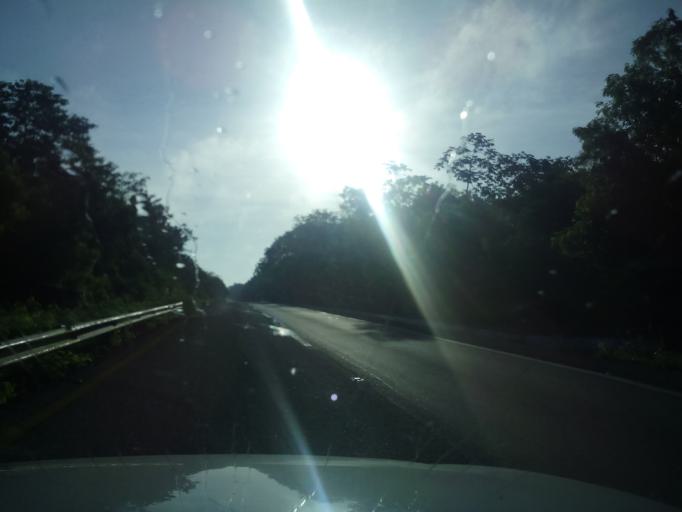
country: MX
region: Yucatan
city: Piste
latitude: 20.7451
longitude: -88.6910
